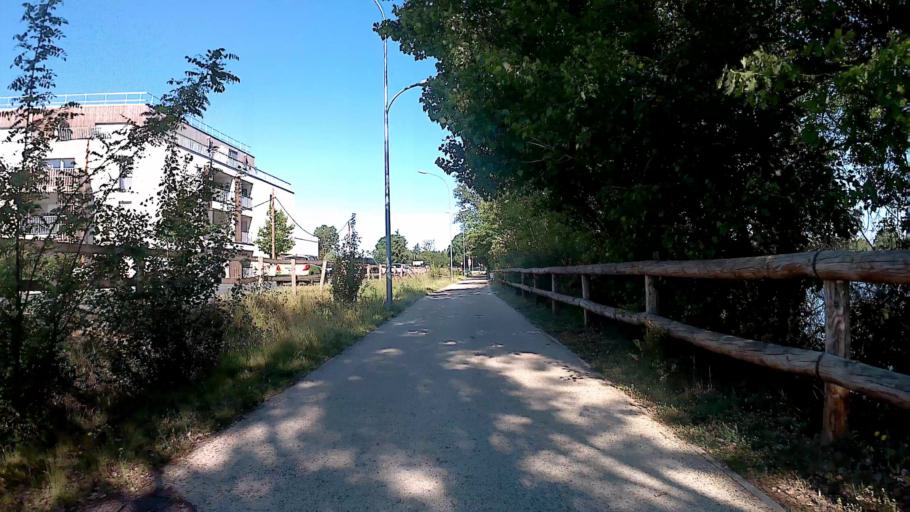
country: FR
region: Aquitaine
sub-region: Departement de la Gironde
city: Villenave-d'Ornon
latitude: 44.7799
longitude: -0.5337
